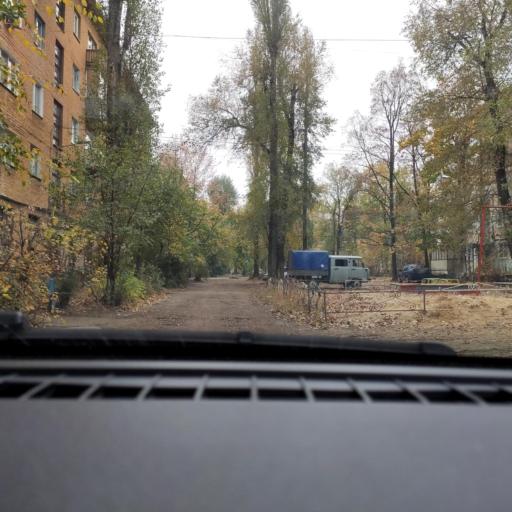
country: RU
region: Voronezj
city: Maslovka
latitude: 51.6072
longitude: 39.2421
